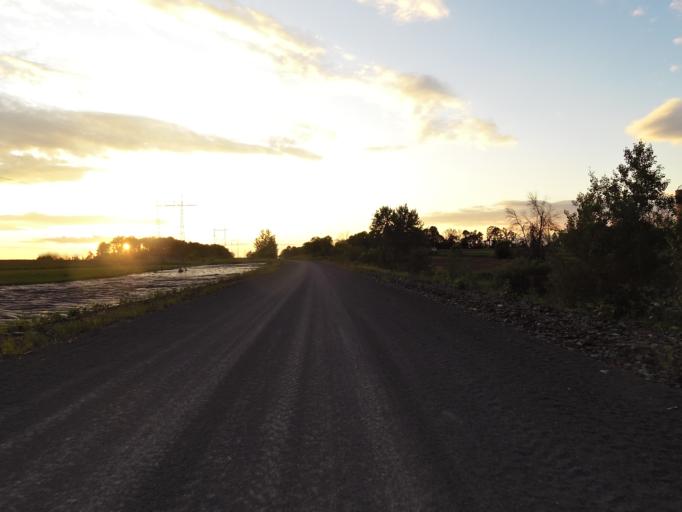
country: CA
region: Ontario
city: Arnprior
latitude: 45.4045
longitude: -76.3266
